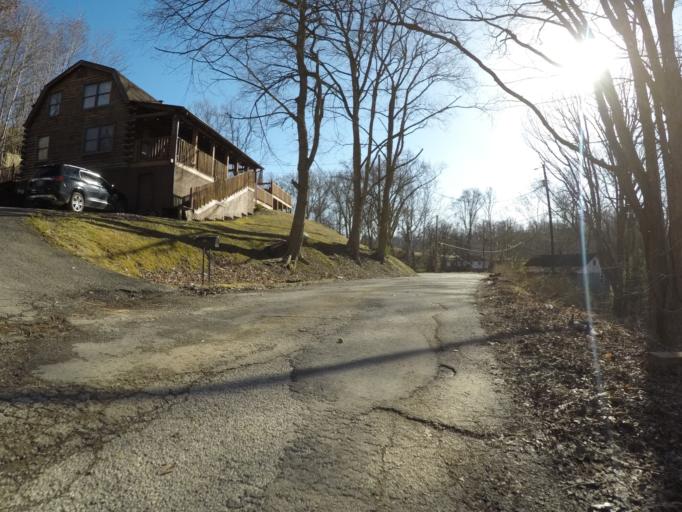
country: US
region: West Virginia
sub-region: Wayne County
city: Ceredo
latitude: 38.3846
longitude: -82.5642
